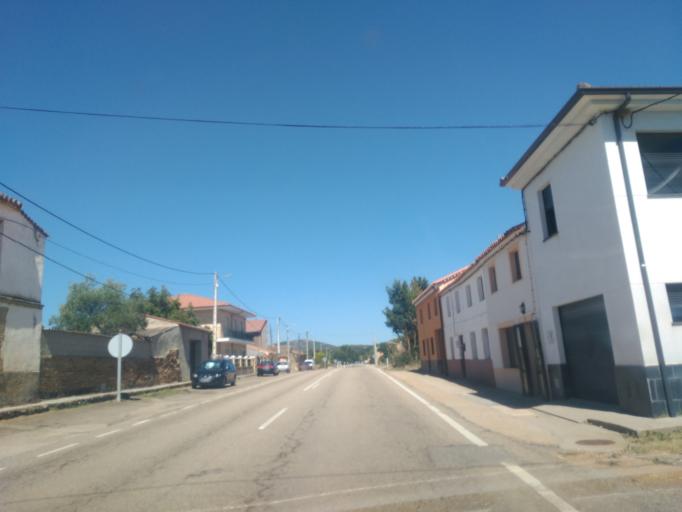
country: ES
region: Castille and Leon
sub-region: Provincia de Zamora
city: Tabara
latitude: 41.8320
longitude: -5.9669
